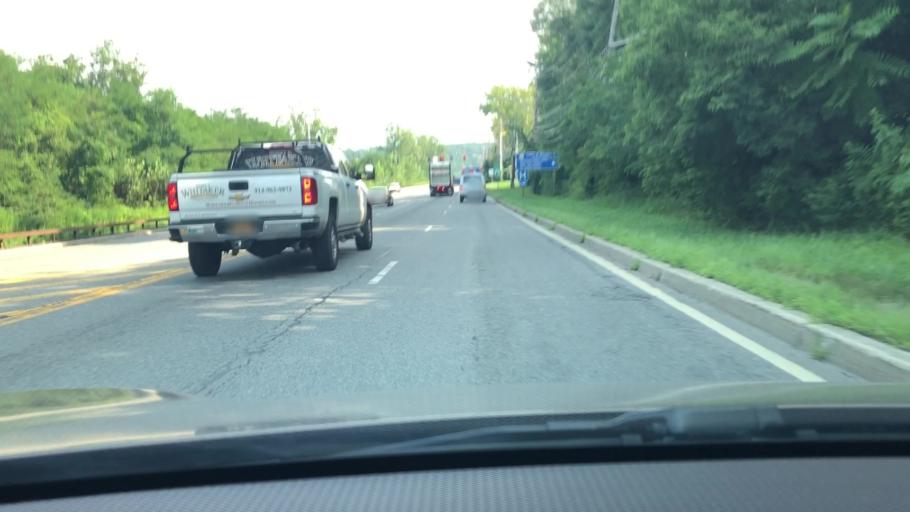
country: US
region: New York
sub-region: Westchester County
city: Elmsford
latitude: 41.0801
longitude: -73.8182
